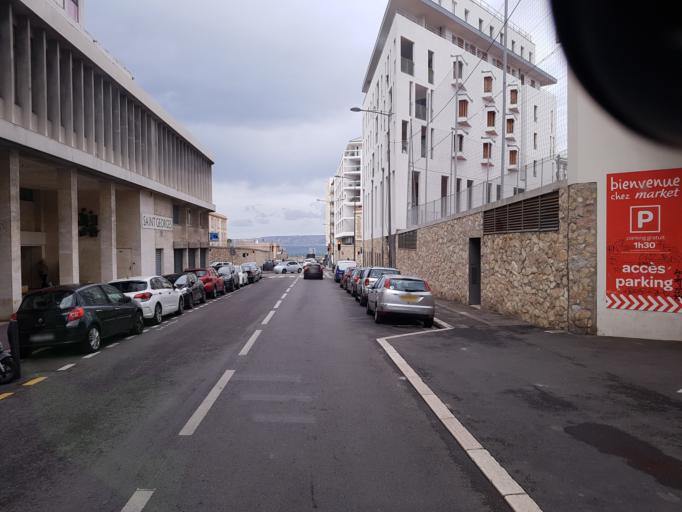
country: FR
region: Provence-Alpes-Cote d'Azur
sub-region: Departement des Bouches-du-Rhone
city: Marseille 07
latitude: 43.2891
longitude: 5.3585
